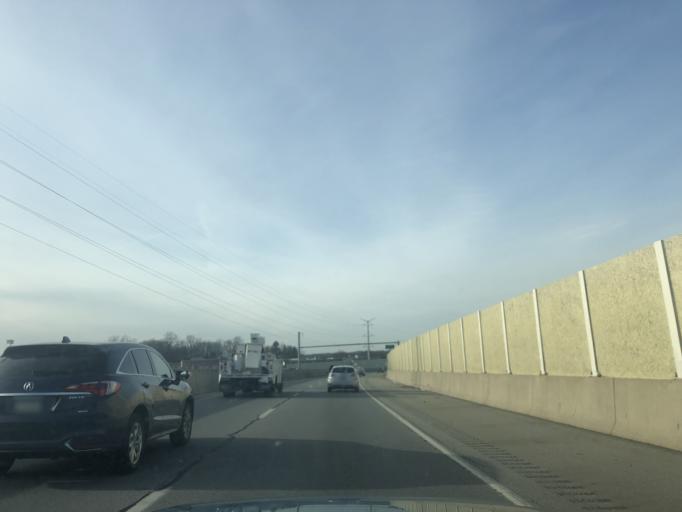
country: US
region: Pennsylvania
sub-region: Montgomery County
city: Flourtown
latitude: 40.1013
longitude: -75.1923
